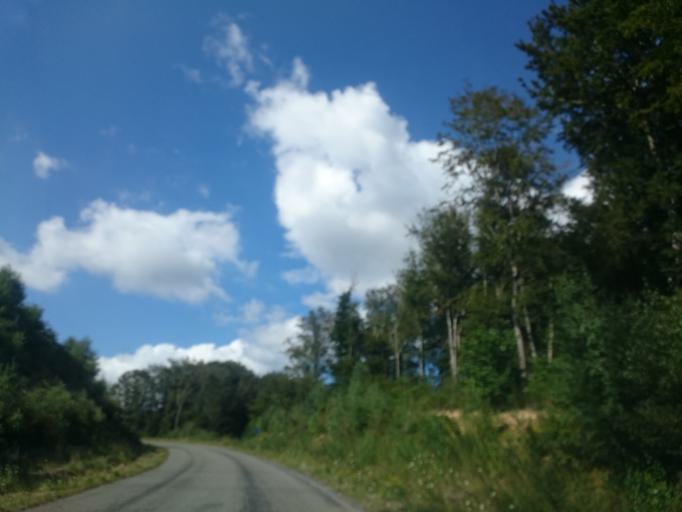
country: FR
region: Auvergne
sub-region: Departement du Cantal
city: Laroquebrou
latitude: 44.8919
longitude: 2.2158
